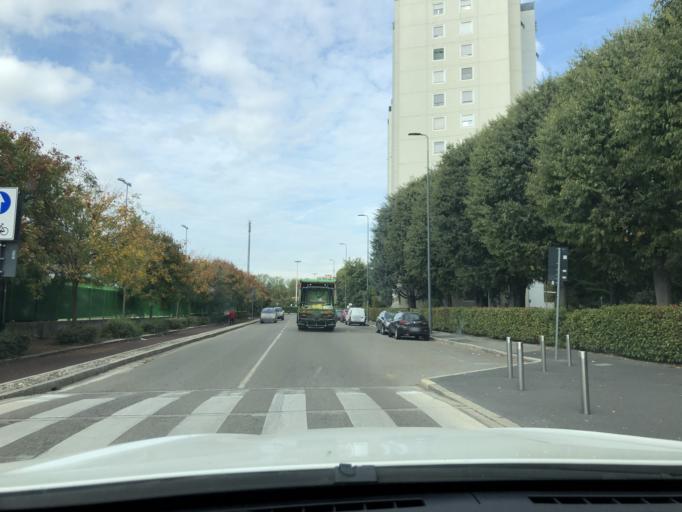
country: IT
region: Lombardy
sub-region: Citta metropolitana di Milano
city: Pero
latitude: 45.4996
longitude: 9.1053
